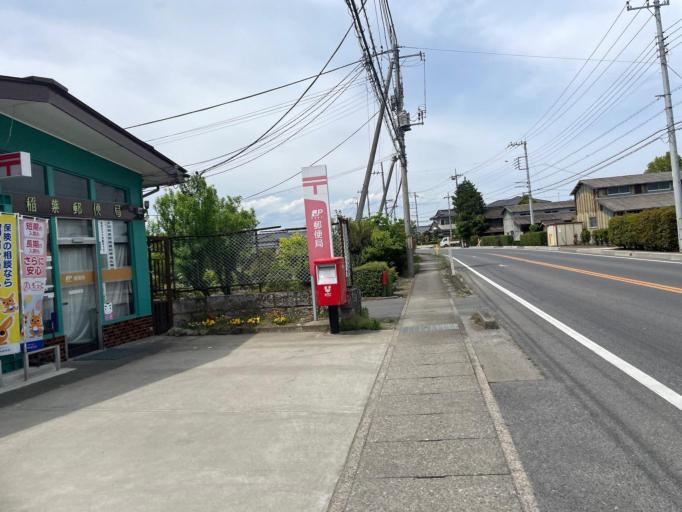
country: JP
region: Tochigi
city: Mibu
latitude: 36.4553
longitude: 139.7747
